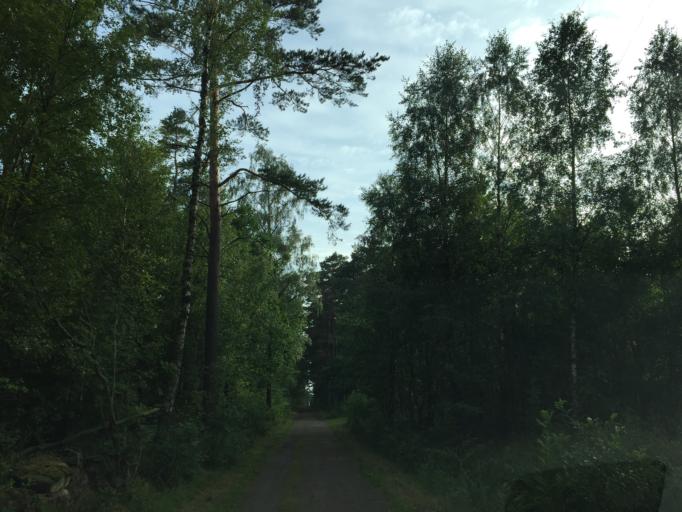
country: SE
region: Halland
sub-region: Falkenbergs Kommun
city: Falkenberg
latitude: 56.8826
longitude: 12.5356
